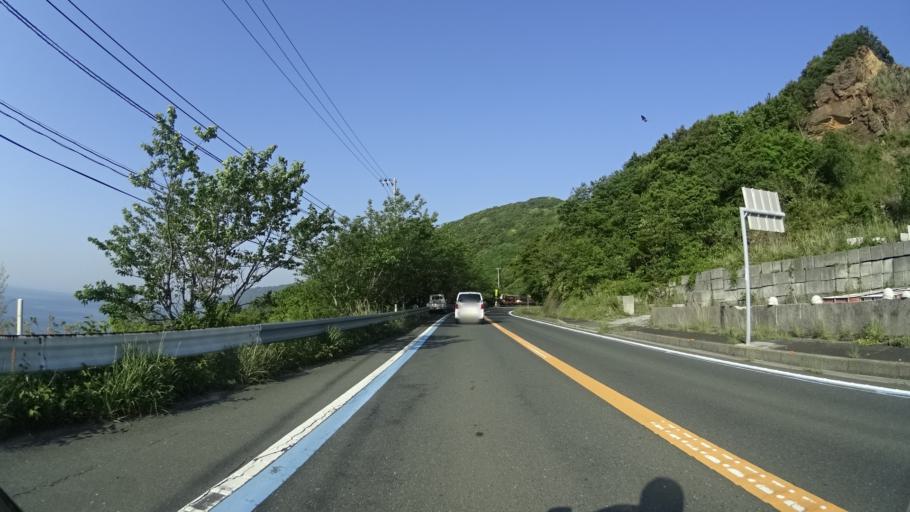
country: JP
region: Ehime
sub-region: Nishiuwa-gun
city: Ikata-cho
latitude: 33.4032
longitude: 132.1693
